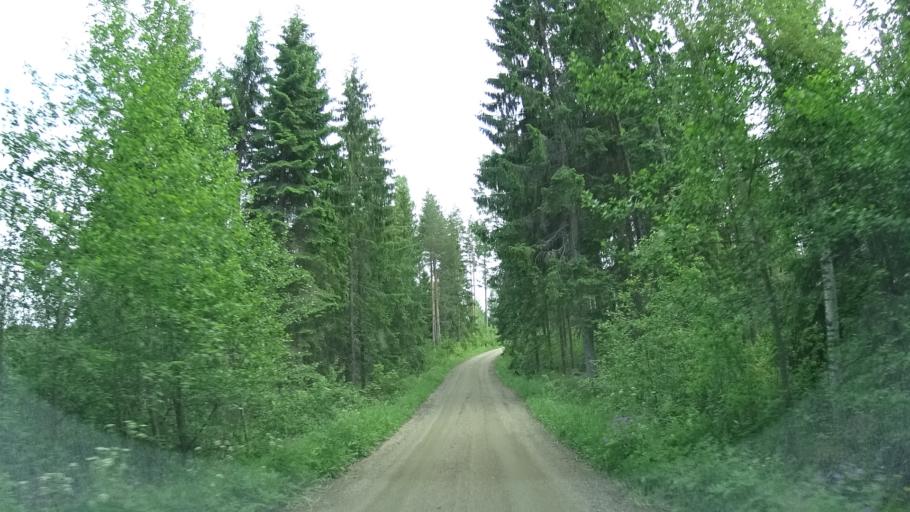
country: FI
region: Central Finland
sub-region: Joutsa
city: Luhanka
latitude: 61.6832
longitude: 25.6863
